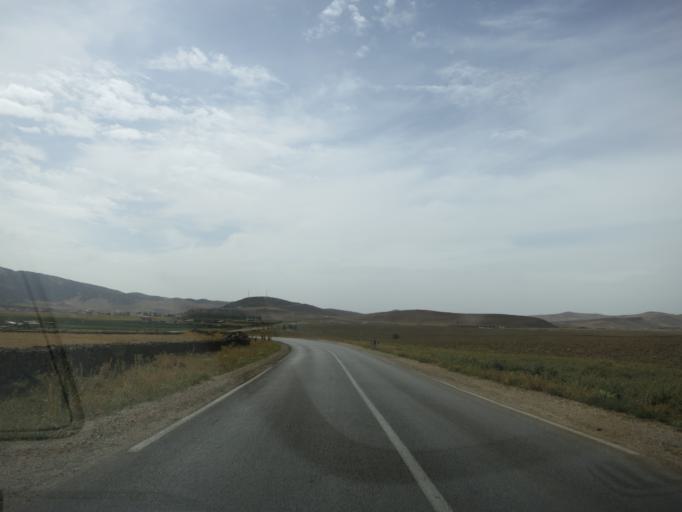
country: MA
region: Meknes-Tafilalet
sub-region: Ifrane
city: Azrou
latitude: 33.2596
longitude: -5.0725
